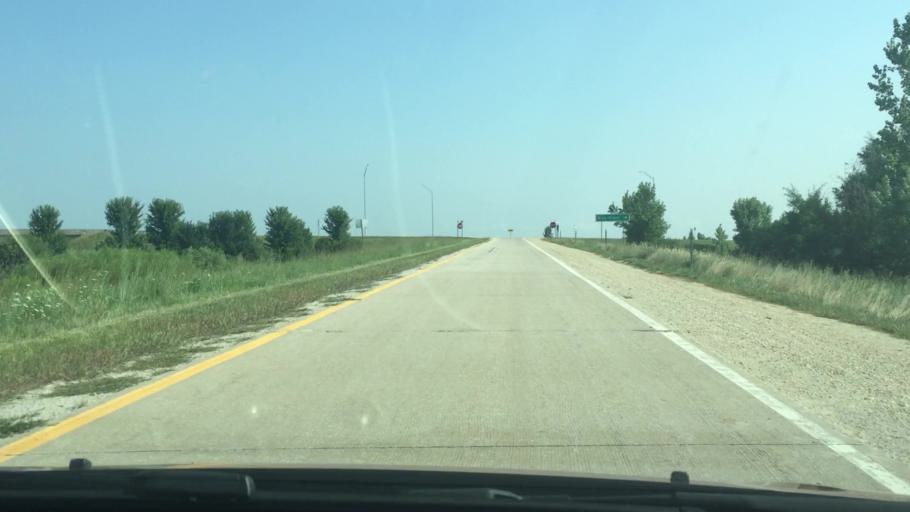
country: US
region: Iowa
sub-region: Scott County
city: Blue Grass
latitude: 41.5125
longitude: -90.7563
